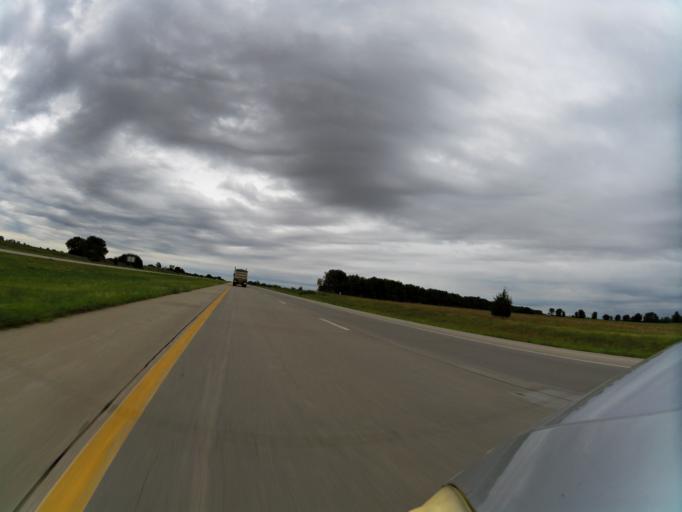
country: US
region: Kansas
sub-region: Reno County
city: Haven
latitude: 37.9341
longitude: -97.8588
